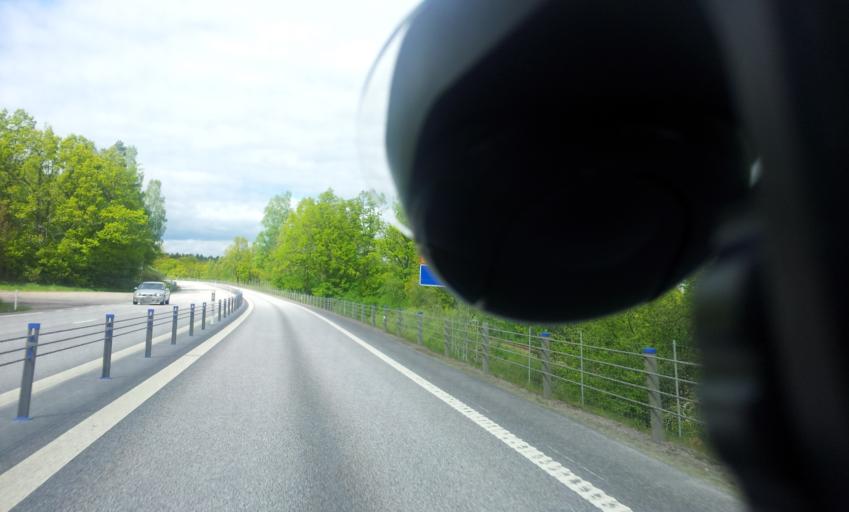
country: SE
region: Kalmar
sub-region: Vasterviks Kommun
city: Gamleby
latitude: 57.8459
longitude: 16.4363
